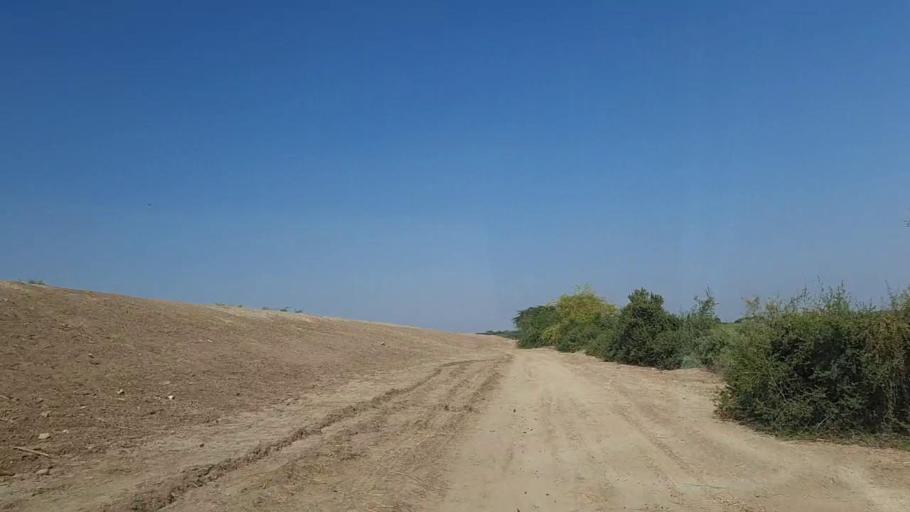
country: PK
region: Sindh
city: Chuhar Jamali
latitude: 24.4845
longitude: 68.0146
